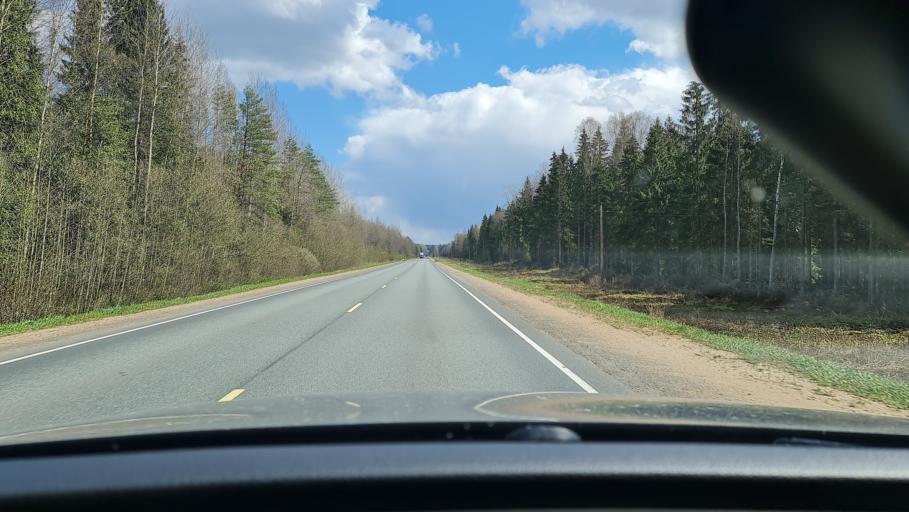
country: RU
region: Tverskaya
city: Zapadnaya Dvina
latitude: 56.3049
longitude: 32.2085
